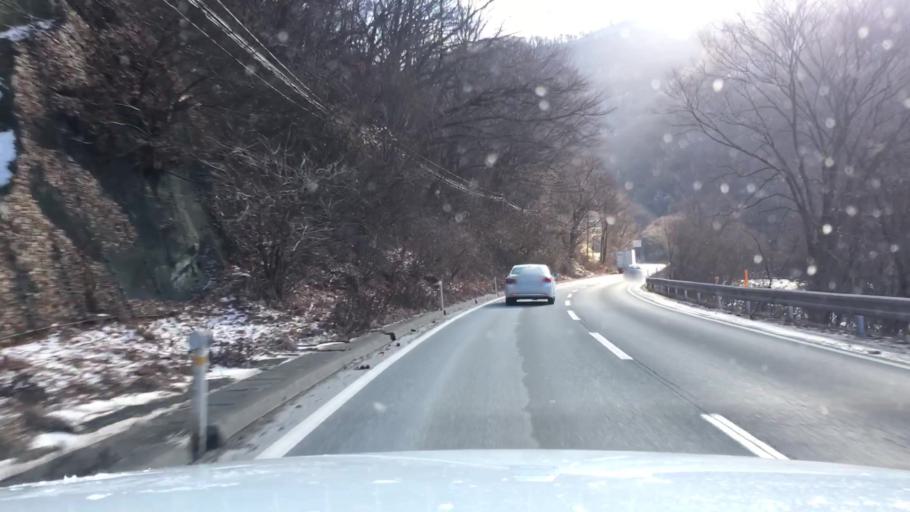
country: JP
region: Iwate
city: Tono
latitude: 39.6191
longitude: 141.4956
